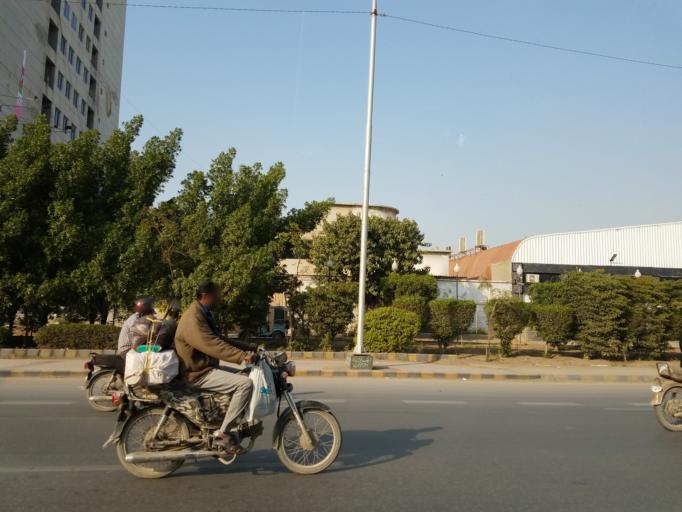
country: PK
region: Sindh
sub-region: Karachi District
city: Karachi
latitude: 24.8597
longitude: 67.0578
